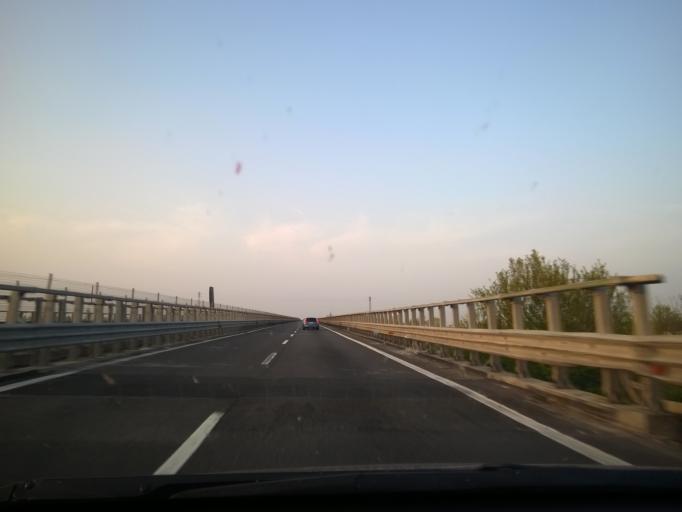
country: IT
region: Veneto
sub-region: Provincia di Padova
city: Boara Pisani
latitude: 45.0925
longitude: 11.7490
